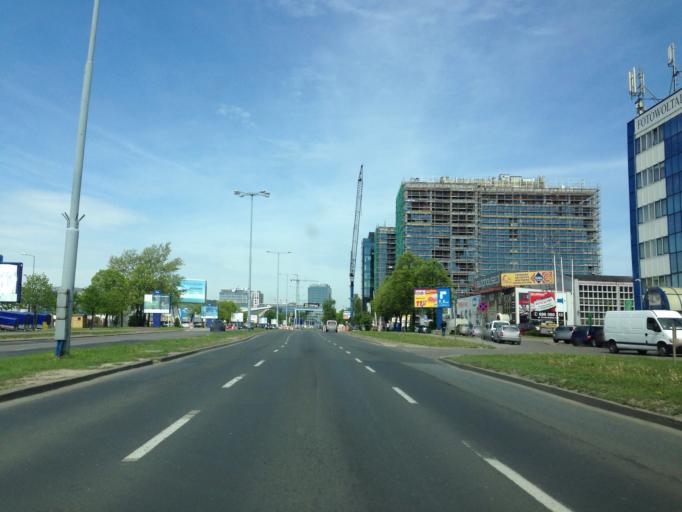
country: PL
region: Pomeranian Voivodeship
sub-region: Sopot
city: Sopot
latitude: 54.3964
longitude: 18.5785
